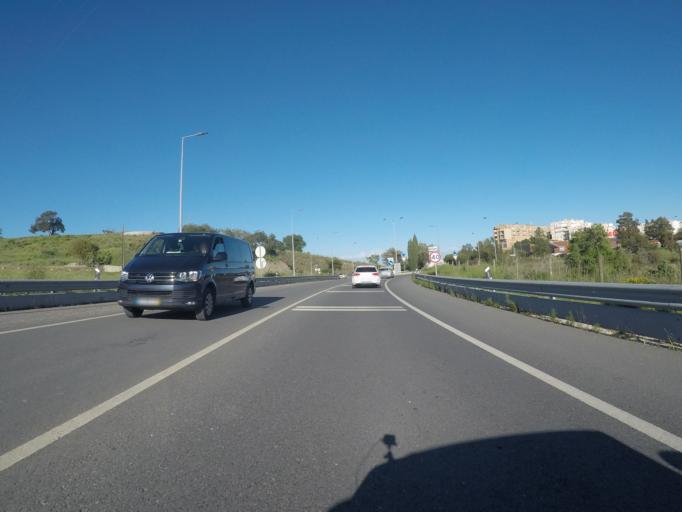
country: PT
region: Faro
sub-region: Lagos
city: Lagos
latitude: 37.1108
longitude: -8.6912
